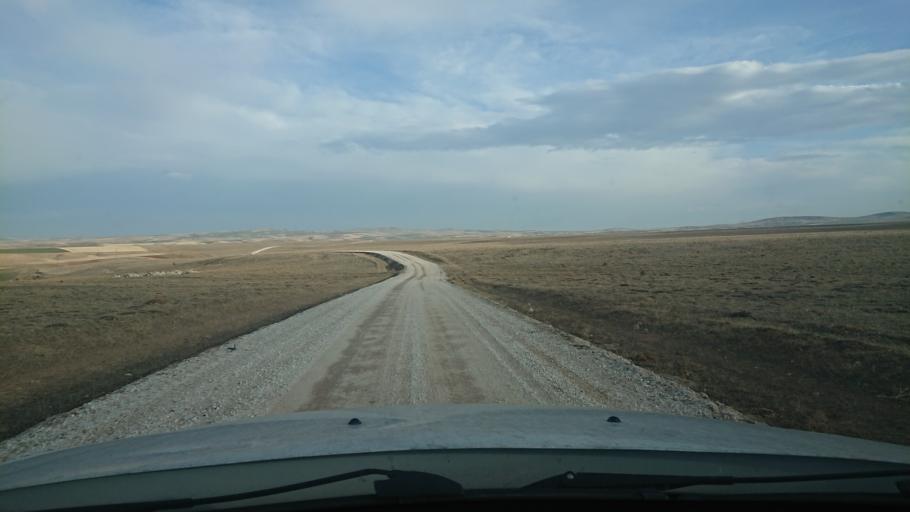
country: TR
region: Aksaray
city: Agacoren
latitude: 38.7288
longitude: 33.8691
